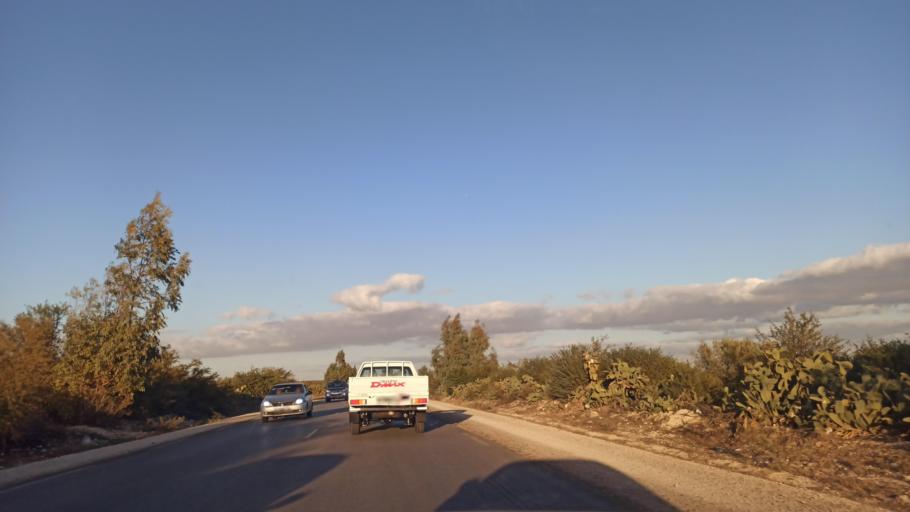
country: TN
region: Al Qayrawan
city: Sbikha
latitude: 35.8583
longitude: 10.2038
